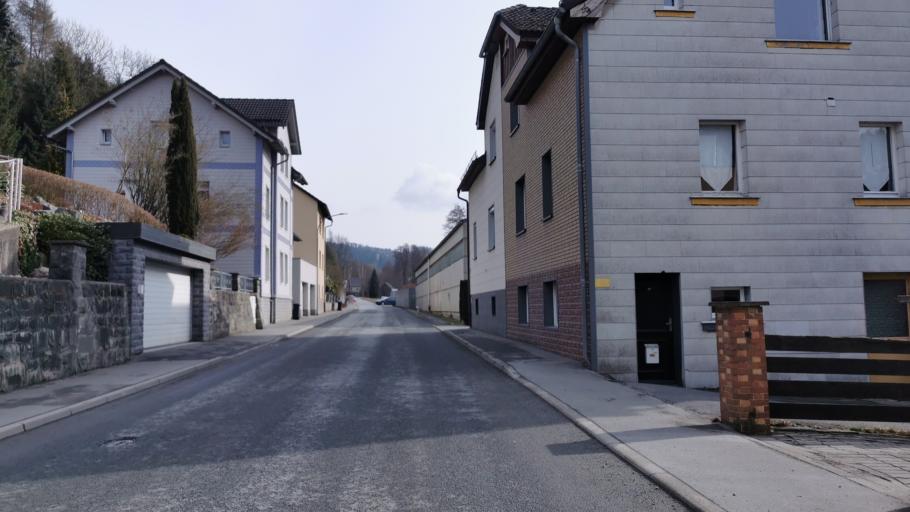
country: DE
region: Bavaria
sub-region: Upper Franconia
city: Ludwigsstadt
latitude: 50.4839
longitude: 11.3942
